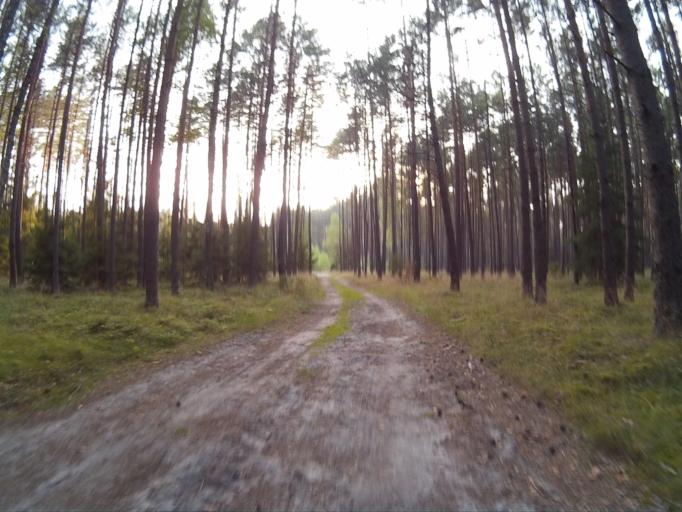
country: PL
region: Pomeranian Voivodeship
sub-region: Powiat chojnicki
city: Czersk
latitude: 53.7219
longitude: 17.8982
